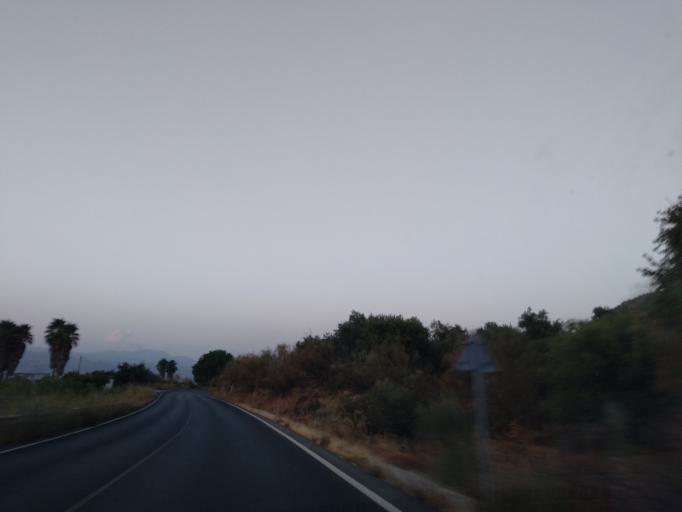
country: ES
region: Andalusia
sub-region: Provincia de Malaga
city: Cartama
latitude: 36.7000
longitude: -4.6480
